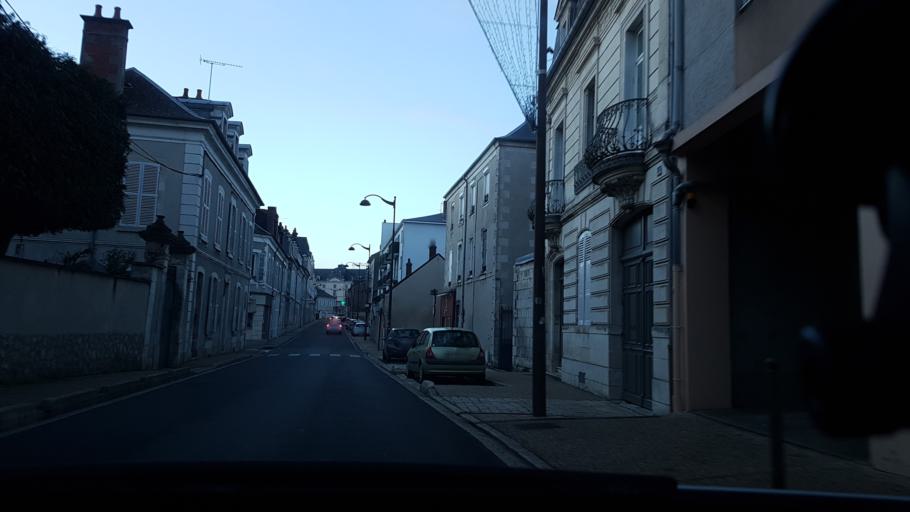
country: FR
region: Centre
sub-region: Departement du Cher
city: Bourges
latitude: 47.0782
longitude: 2.4018
